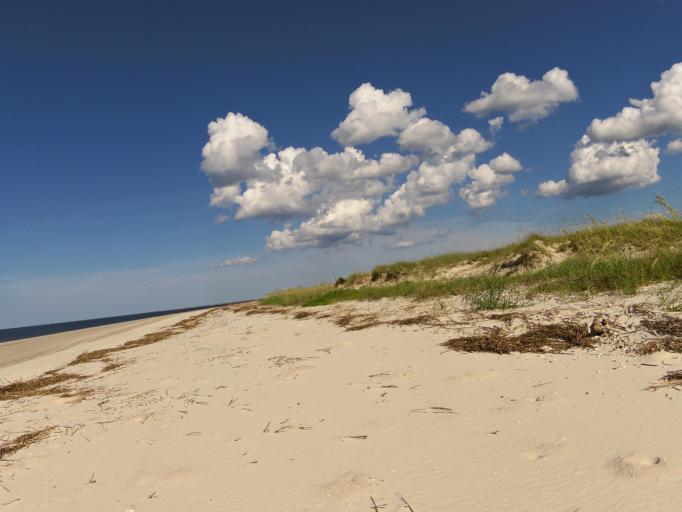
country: US
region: Florida
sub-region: Nassau County
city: Fernandina Beach
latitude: 30.7041
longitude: -81.4358
